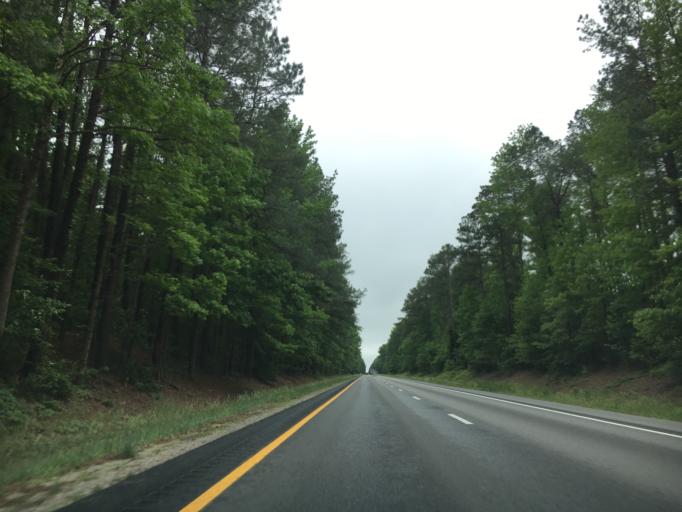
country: US
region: Virginia
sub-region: Dinwiddie County
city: Dinwiddie
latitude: 37.0449
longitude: -77.6195
